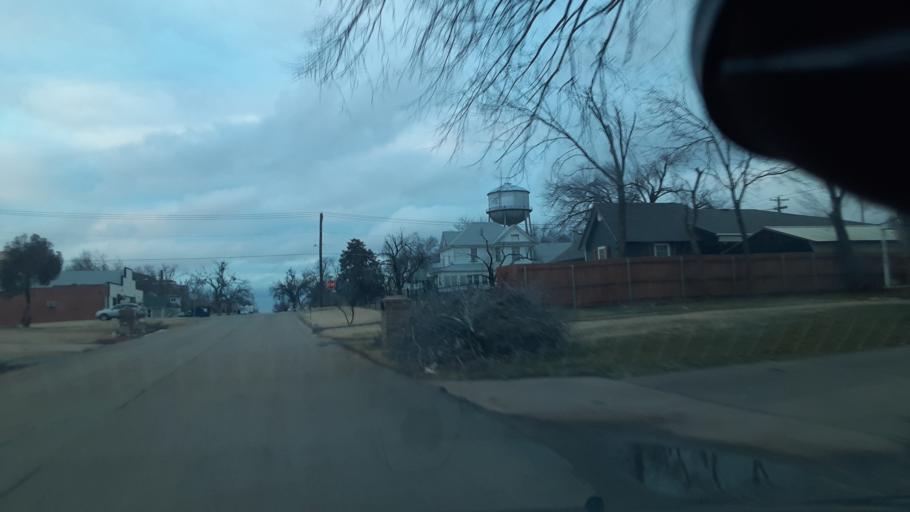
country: US
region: Oklahoma
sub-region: Logan County
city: Guthrie
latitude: 35.8754
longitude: -97.4124
